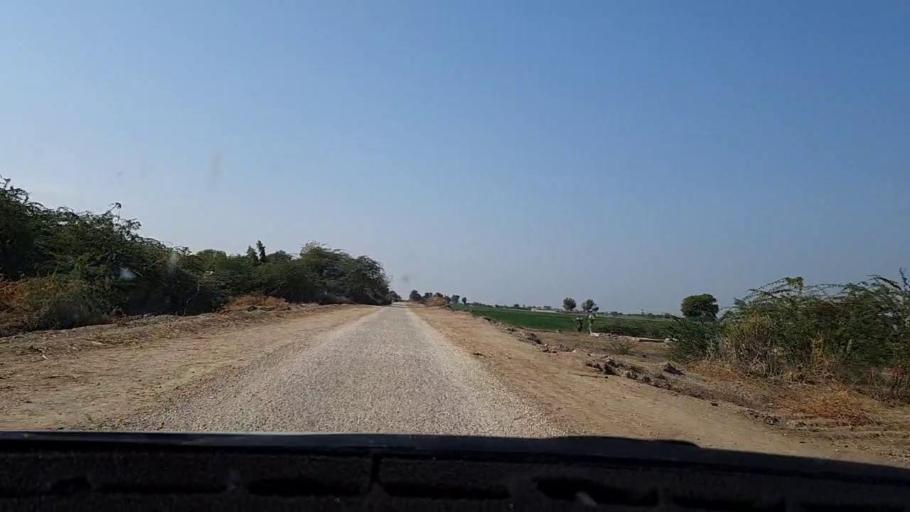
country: PK
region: Sindh
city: Tando Mittha Khan
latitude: 25.8156
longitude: 69.3055
